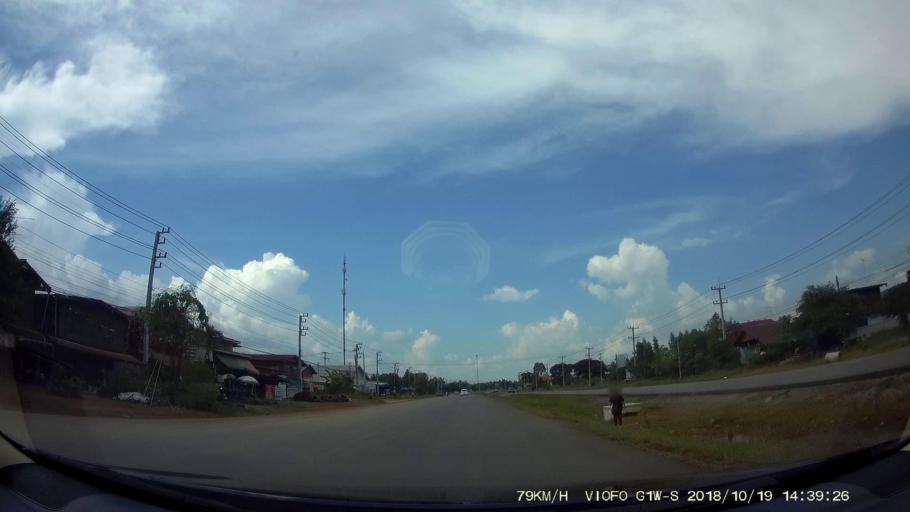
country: TH
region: Chaiyaphum
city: Kaeng Khro
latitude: 16.2260
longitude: 102.1951
